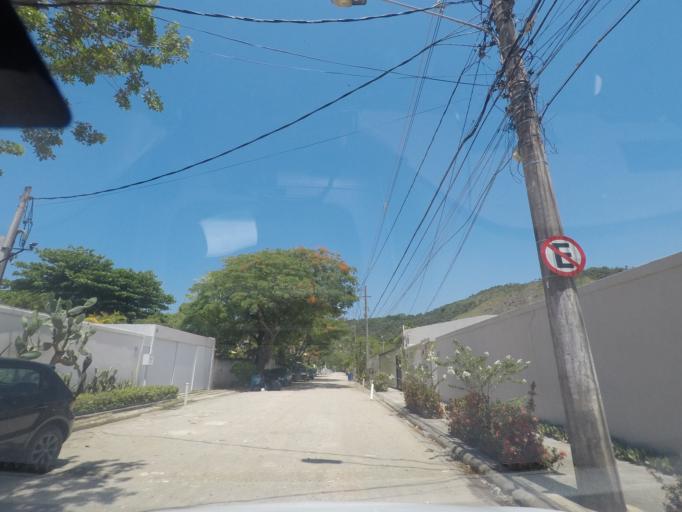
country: BR
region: Rio de Janeiro
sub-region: Niteroi
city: Niteroi
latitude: -22.9732
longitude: -43.0328
